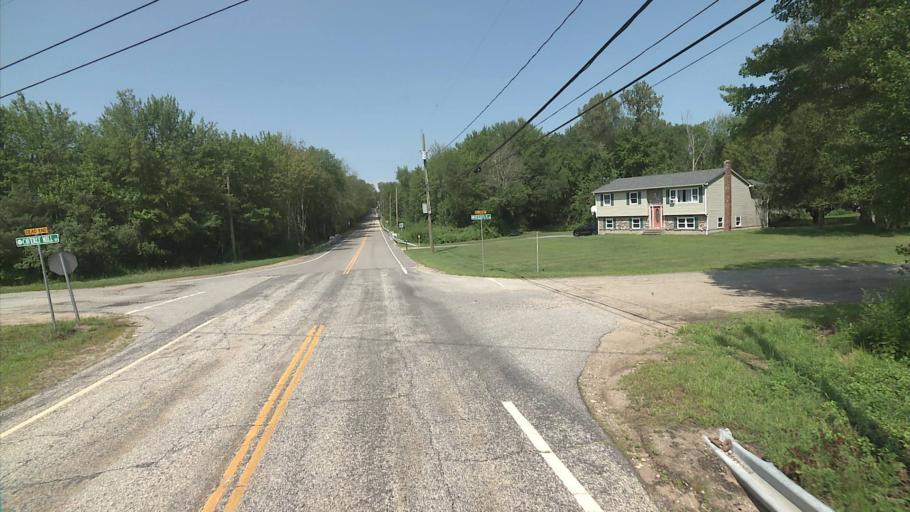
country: US
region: Connecticut
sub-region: New London County
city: Colchester
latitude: 41.5742
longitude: -72.2738
